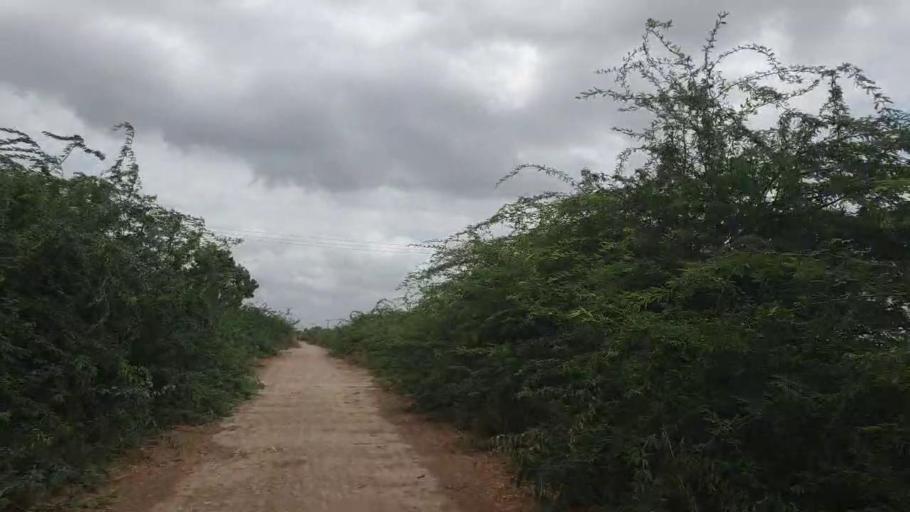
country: PK
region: Sindh
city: Badin
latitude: 24.6285
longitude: 68.9468
